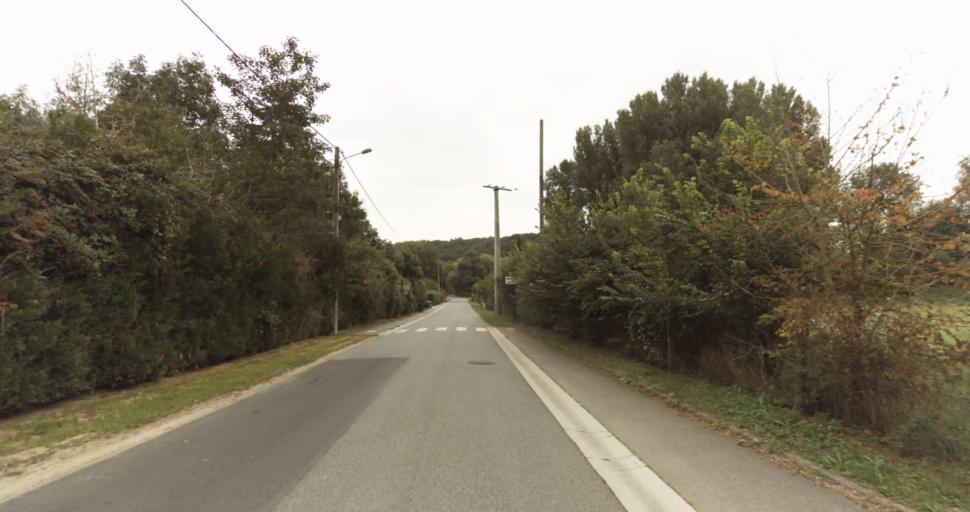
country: FR
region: Haute-Normandie
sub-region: Departement de l'Eure
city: Marcilly-sur-Eure
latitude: 48.8208
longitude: 1.3569
